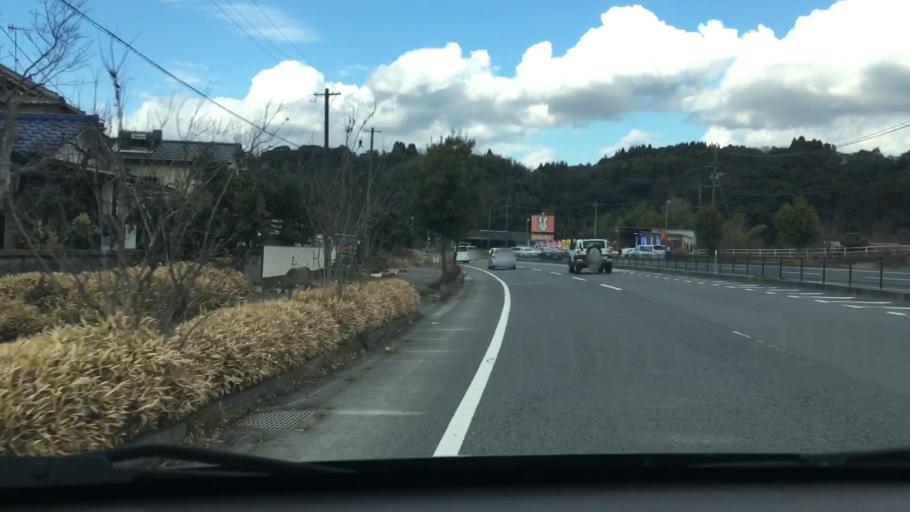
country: JP
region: Oita
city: Oita
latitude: 33.1327
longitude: 131.6598
